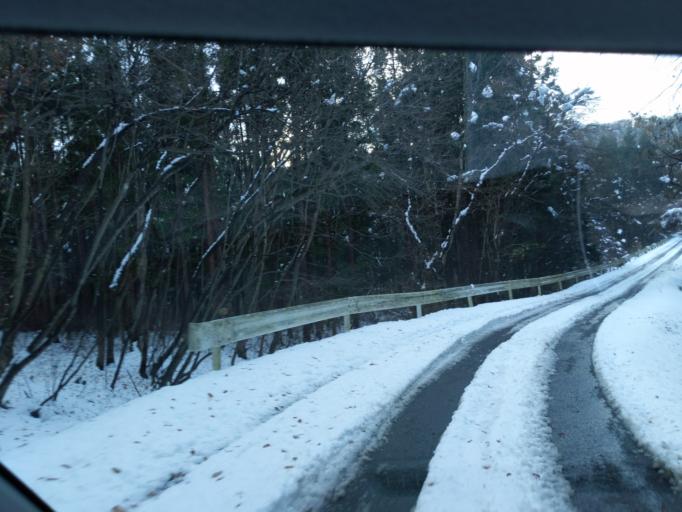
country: JP
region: Iwate
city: Mizusawa
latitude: 39.0523
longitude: 141.0591
